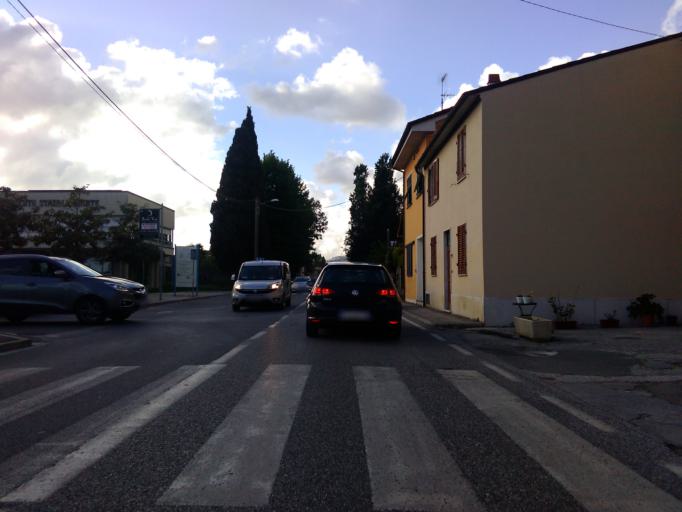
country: IT
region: Tuscany
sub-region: Provincia di Lucca
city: Pietrasanta
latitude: 43.9632
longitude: 10.2247
